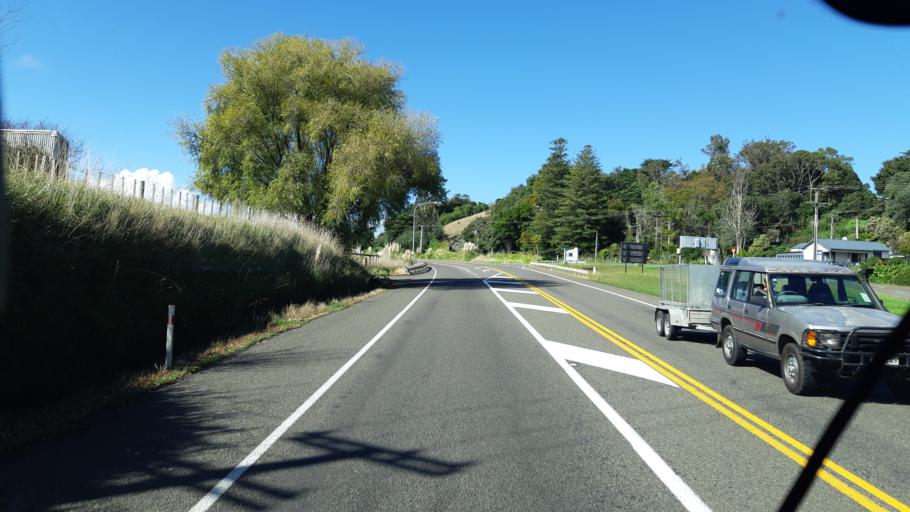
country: NZ
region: Manawatu-Wanganui
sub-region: Wanganui District
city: Wanganui
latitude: -39.9547
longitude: 175.0658
